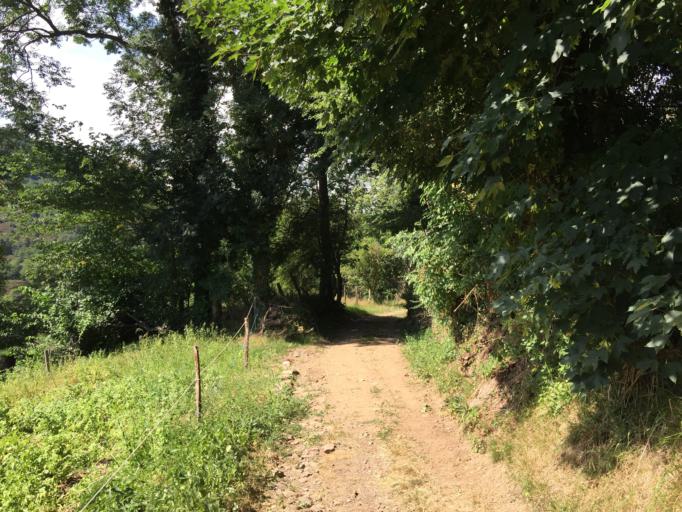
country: FR
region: Rhone-Alpes
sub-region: Departement de la Loire
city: Saint-Chamond
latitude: 45.4183
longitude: 4.5149
